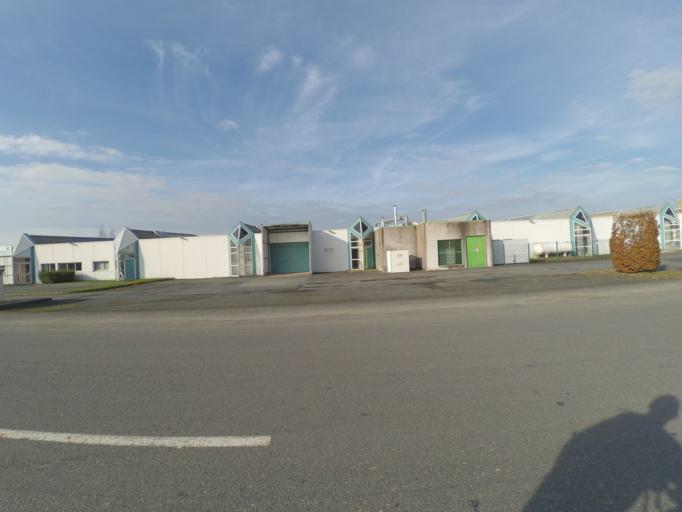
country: FR
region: Pays de la Loire
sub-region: Departement de la Vendee
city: Saint-Hilaire-de-Loulay
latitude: 47.0242
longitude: -1.3466
